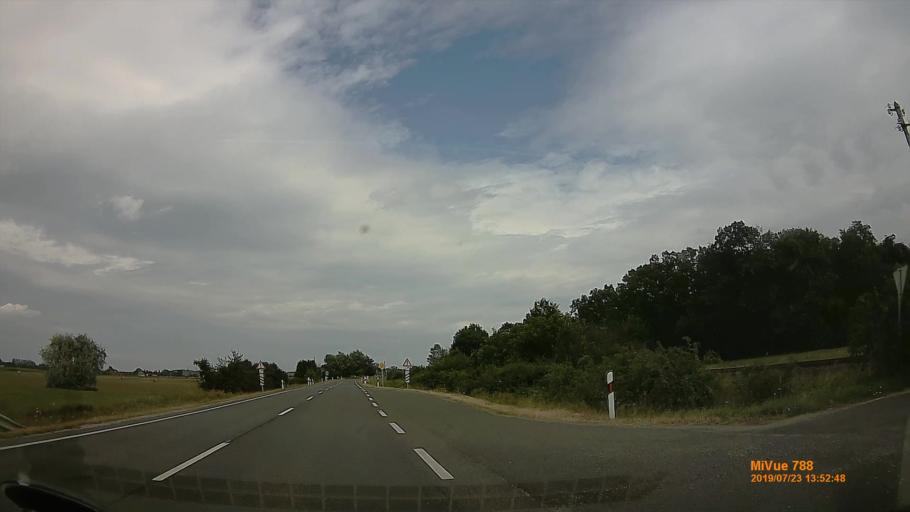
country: HU
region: Hajdu-Bihar
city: Polgar
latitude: 47.9062
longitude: 21.1657
